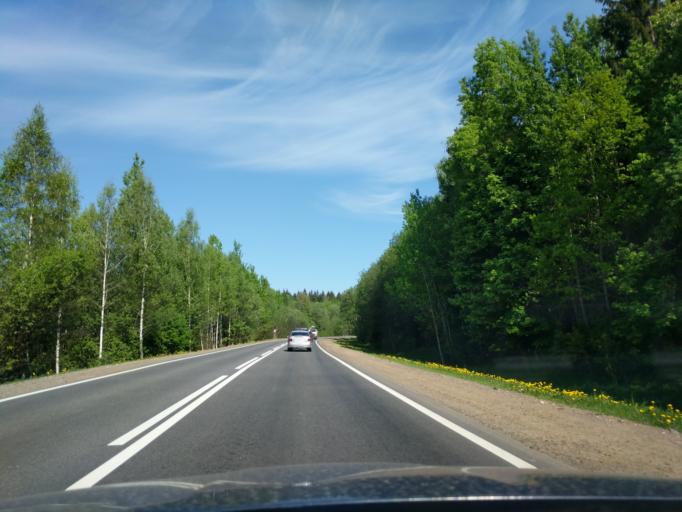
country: BY
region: Minsk
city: Bal'shavik
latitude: 54.1044
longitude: 27.5305
